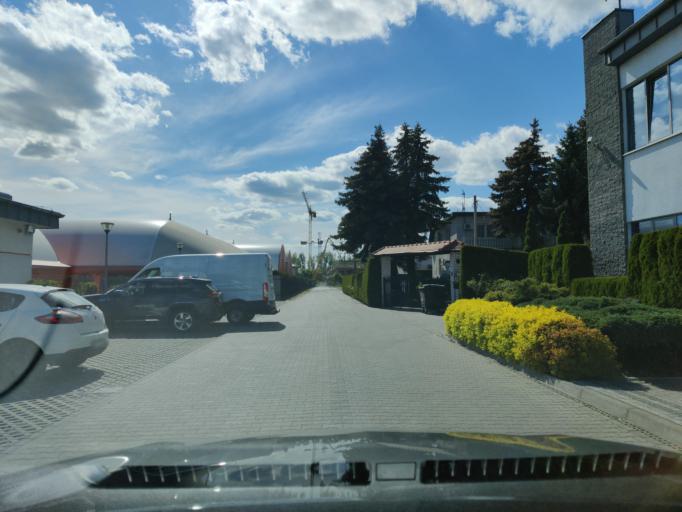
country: PL
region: Masovian Voivodeship
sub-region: Powiat legionowski
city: Stanislawow Pierwszy
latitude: 52.3376
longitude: 21.0278
